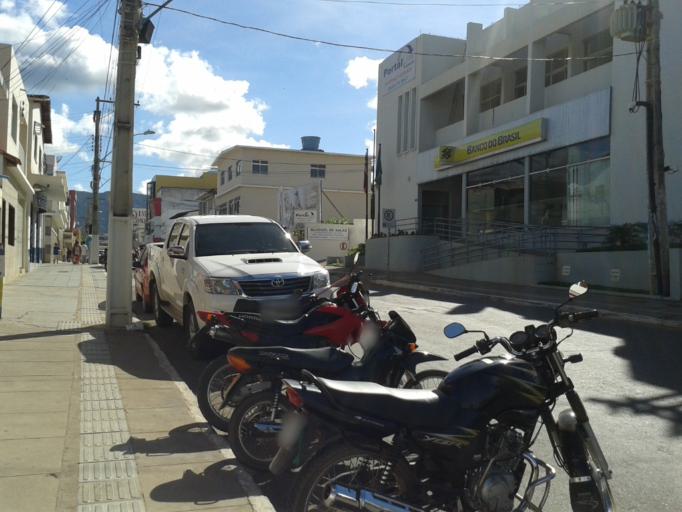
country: BR
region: Bahia
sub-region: Livramento Do Brumado
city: Livramento do Brumado
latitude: -13.6507
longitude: -41.8427
